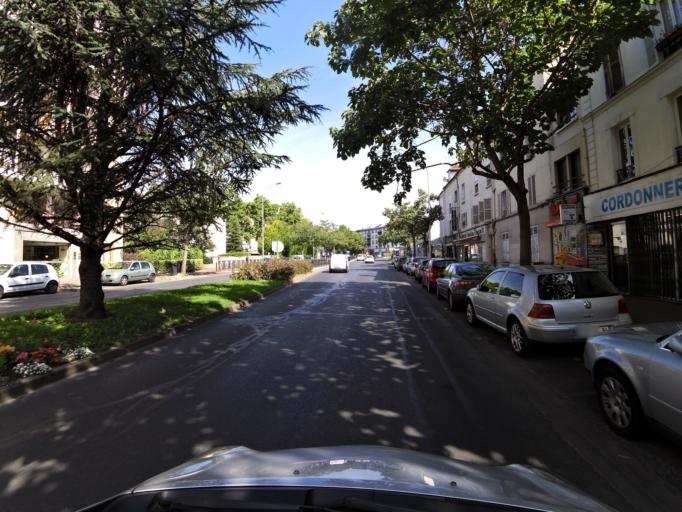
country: FR
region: Ile-de-France
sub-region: Departement du Val-de-Marne
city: Joinville-le-Pont
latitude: 48.8085
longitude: 2.4713
